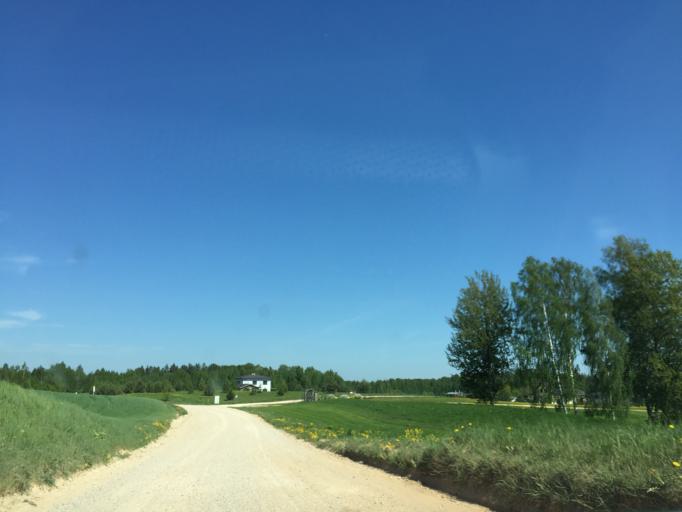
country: LV
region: Ikskile
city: Ikskile
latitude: 56.8673
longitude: 24.5022
